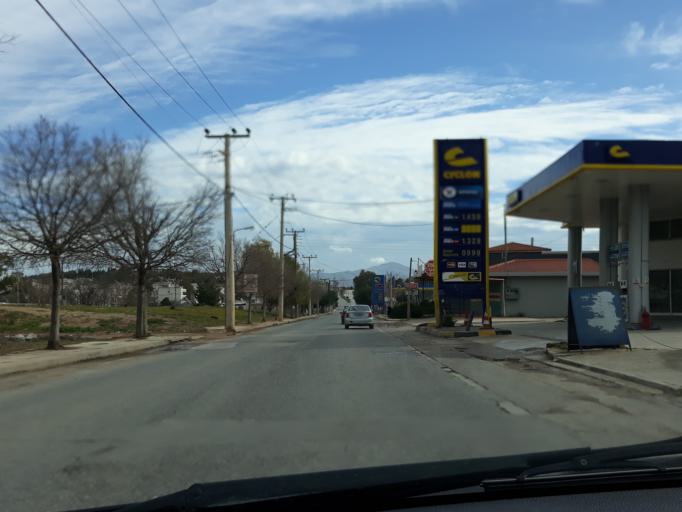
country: GR
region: Attica
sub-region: Nomarchia Dytikis Attikis
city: Ano Liosia
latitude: 38.0799
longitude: 23.7134
